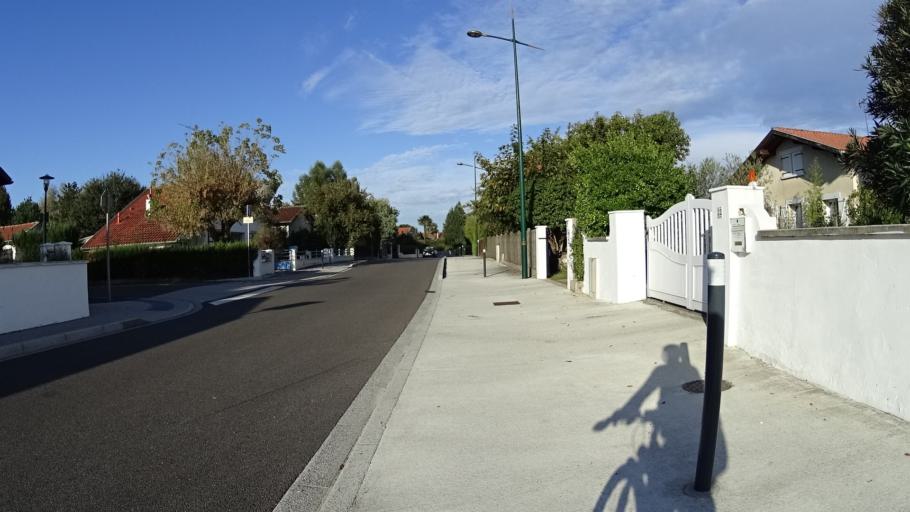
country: FR
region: Aquitaine
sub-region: Departement des Landes
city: Saint-Paul-les-Dax
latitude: 43.7299
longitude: -1.0583
